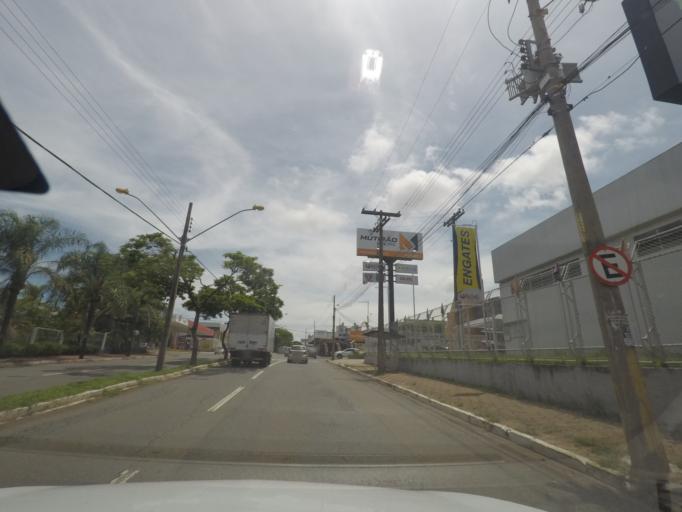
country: BR
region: Goias
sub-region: Goiania
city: Goiania
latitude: -16.6853
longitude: -49.2942
